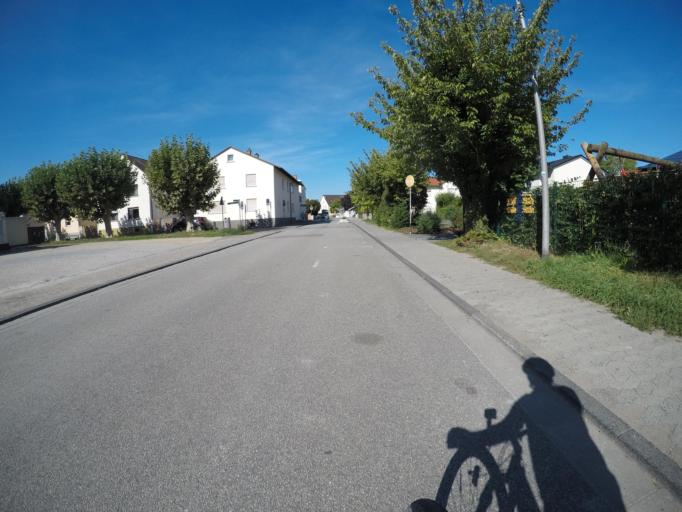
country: DE
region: Hesse
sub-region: Regierungsbezirk Darmstadt
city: Stockstadt am Rhein
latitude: 49.8105
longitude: 8.4691
